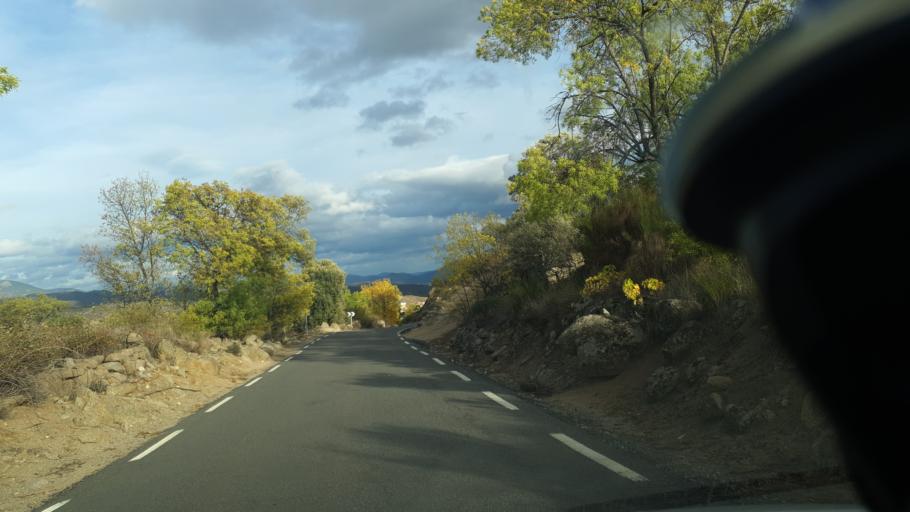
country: ES
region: Castille and Leon
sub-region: Provincia de Avila
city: Burgohondo
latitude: 40.4118
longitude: -4.8104
